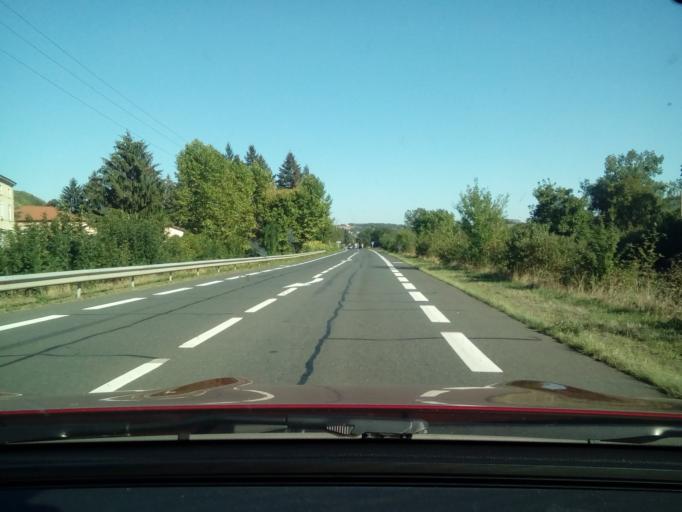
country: FR
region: Rhone-Alpes
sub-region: Departement du Rhone
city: Chatillon
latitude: 45.8883
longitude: 4.6150
